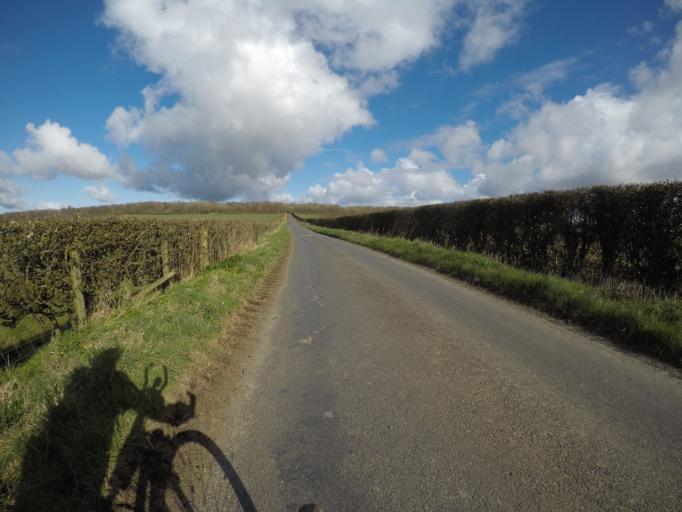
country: GB
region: Scotland
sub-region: North Ayrshire
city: Irvine
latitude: 55.6687
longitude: -4.6512
